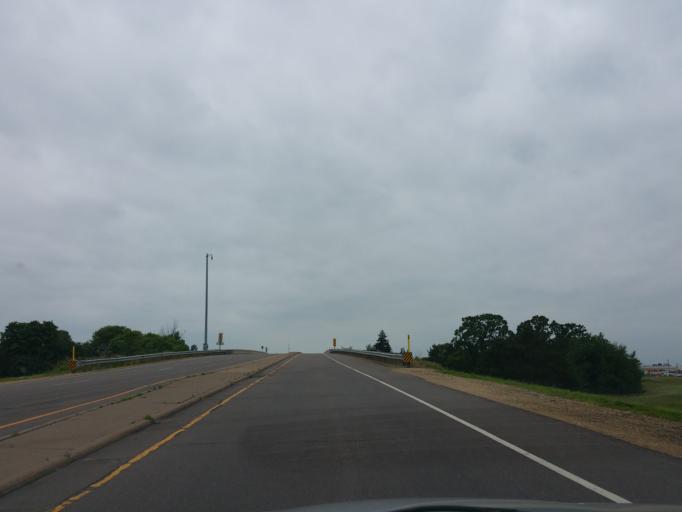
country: US
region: Wisconsin
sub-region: Eau Claire County
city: Eau Claire
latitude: 44.8435
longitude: -91.6021
